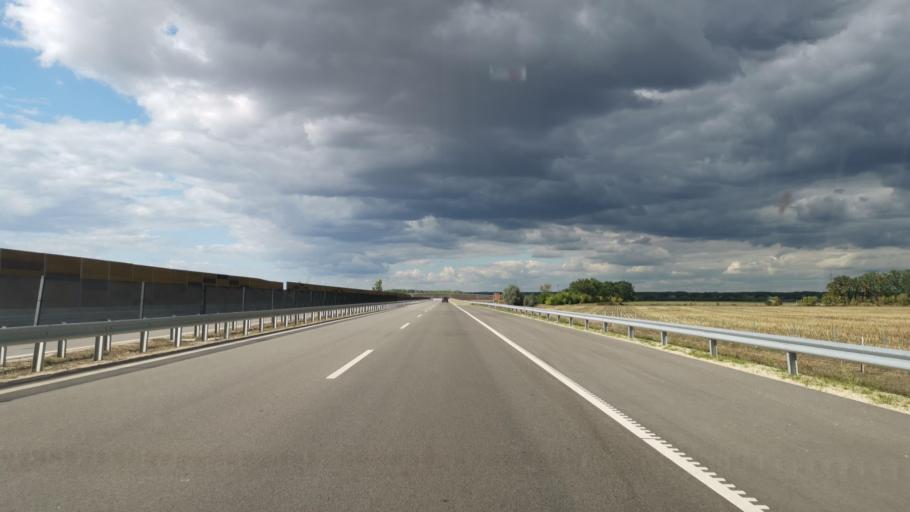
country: HU
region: Jasz-Nagykun-Szolnok
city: Tiszapuspoki
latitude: 47.1968
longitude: 20.3318
